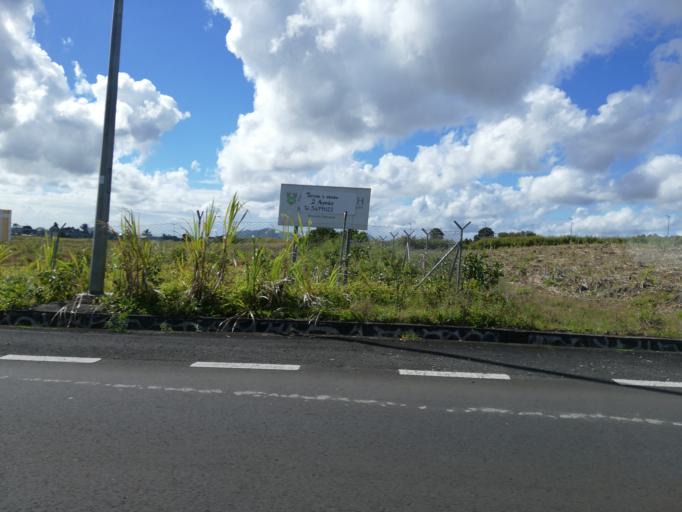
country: MU
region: Moka
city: Quartier Militaire
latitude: -20.2526
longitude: 57.5852
